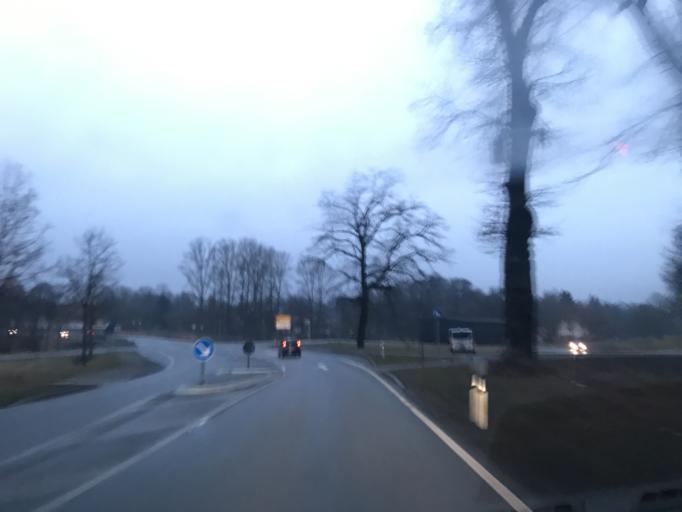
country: DE
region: Hesse
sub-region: Regierungsbezirk Kassel
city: Hofgeismar
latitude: 51.5033
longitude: 9.4109
